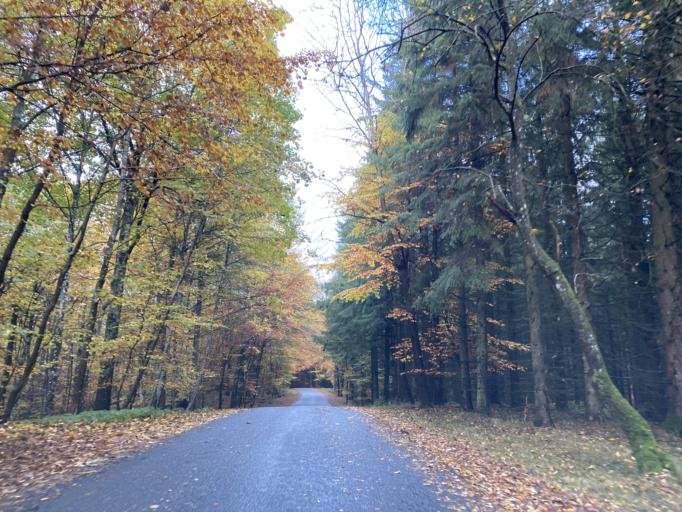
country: DK
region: Central Jutland
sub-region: Skanderborg Kommune
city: Galten
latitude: 56.2272
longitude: 9.9287
